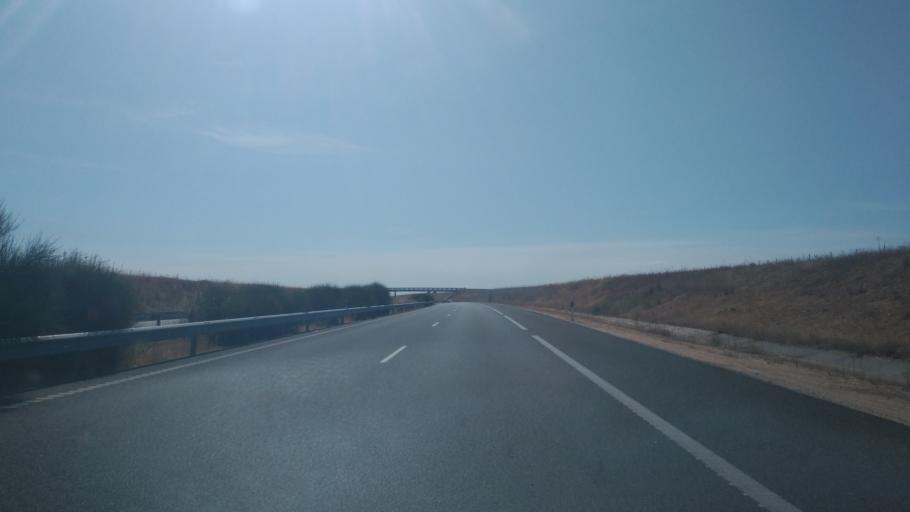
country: ES
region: Castille and Leon
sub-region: Provincia de Salamanca
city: Machacon
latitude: 40.9240
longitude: -5.5351
